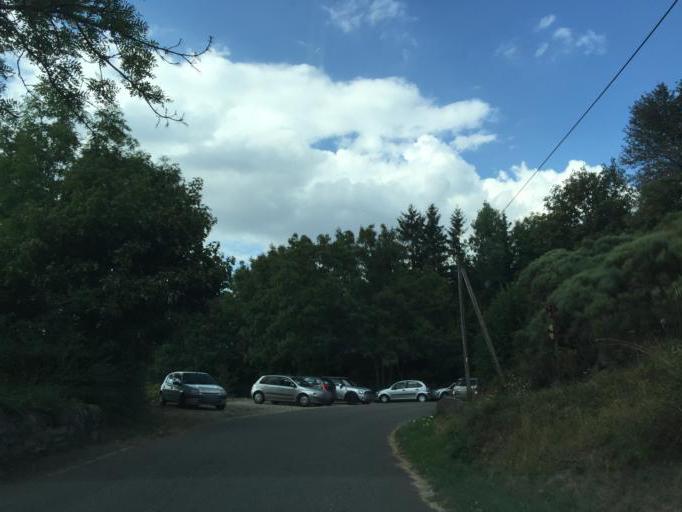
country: FR
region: Rhone-Alpes
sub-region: Departement de la Loire
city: Saint-Jean-Bonnefonds
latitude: 45.4060
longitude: 4.4461
